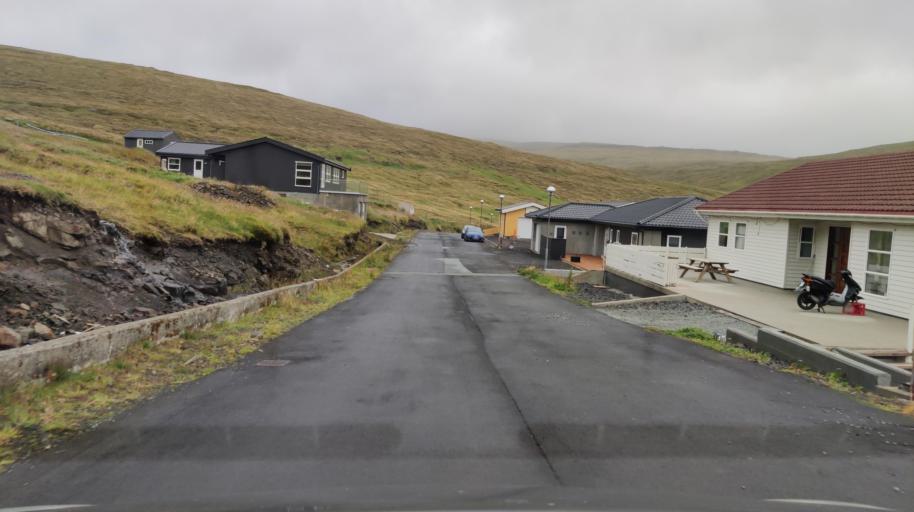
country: FO
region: Streymoy
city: Vestmanna
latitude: 62.1539
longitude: -7.1850
